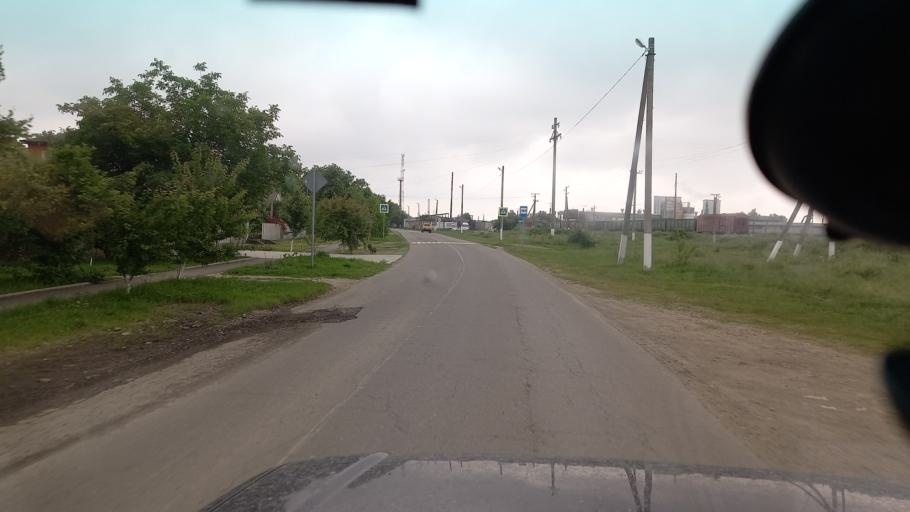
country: RU
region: Krasnodarskiy
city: Mostovskoy
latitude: 44.4210
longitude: 40.7759
